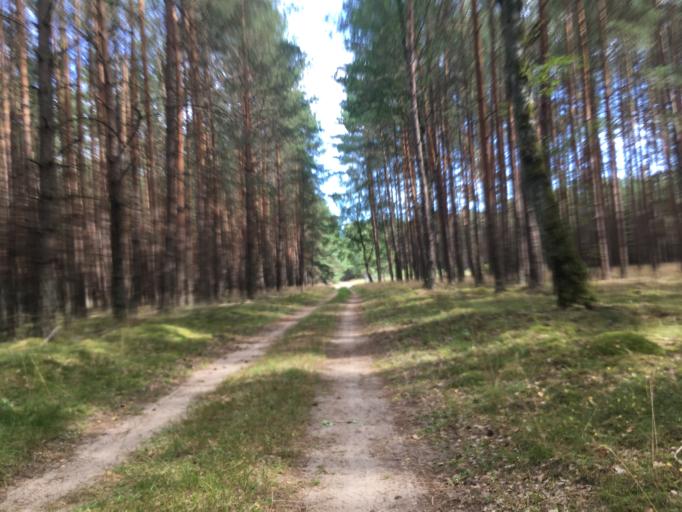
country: DE
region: Brandenburg
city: Rheinsberg
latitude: 53.0354
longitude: 12.9219
